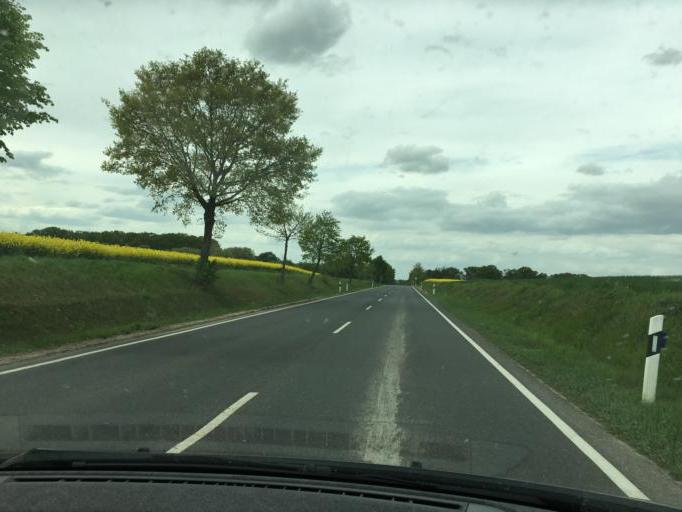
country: DE
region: North Rhine-Westphalia
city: Zulpich
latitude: 50.7259
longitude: 6.6786
